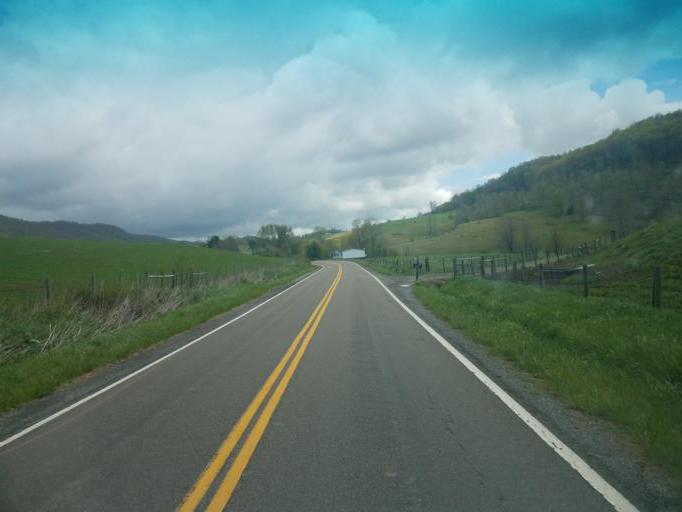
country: US
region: Virginia
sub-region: Smyth County
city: Atkins
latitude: 36.9961
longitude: -81.3795
